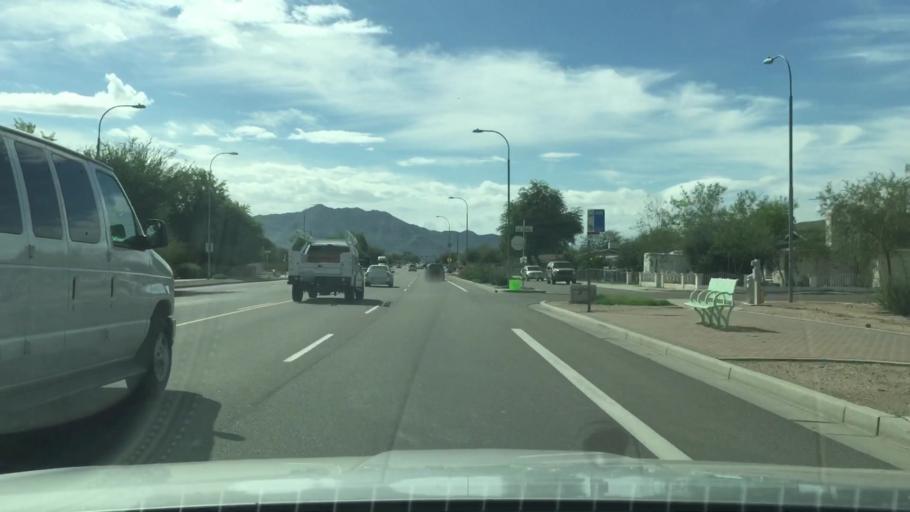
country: US
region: Arizona
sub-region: Maricopa County
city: Laveen
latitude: 33.3975
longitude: -112.1337
